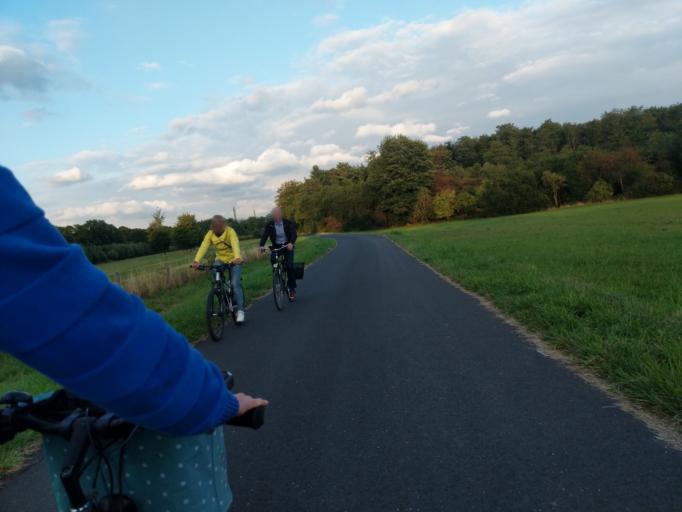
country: DE
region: North Rhine-Westphalia
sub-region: Regierungsbezirk Dusseldorf
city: Krefeld
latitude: 51.3345
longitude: 6.6529
